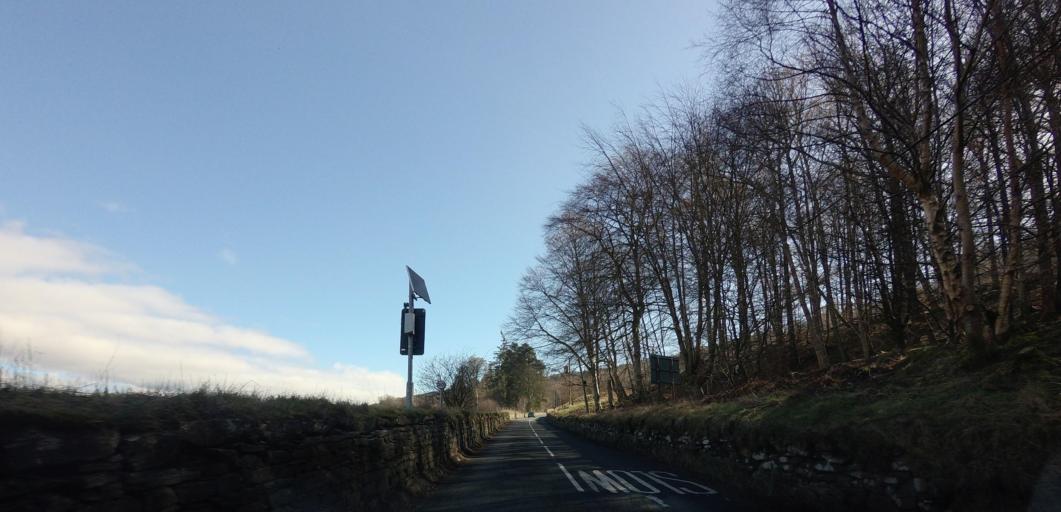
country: GB
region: Scotland
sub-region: Perth and Kinross
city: Aberfeldy
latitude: 56.5826
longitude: -3.9937
